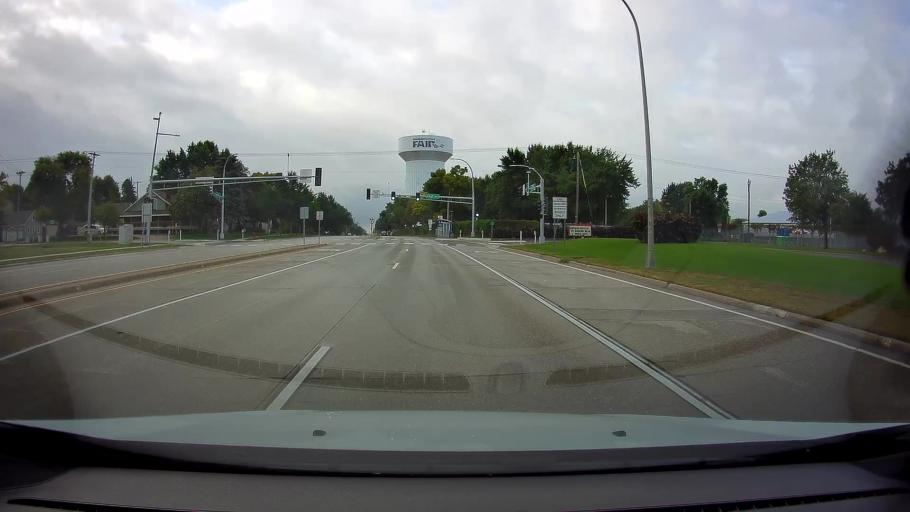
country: US
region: Minnesota
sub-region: Ramsey County
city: Falcon Heights
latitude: 44.9888
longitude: -93.1670
